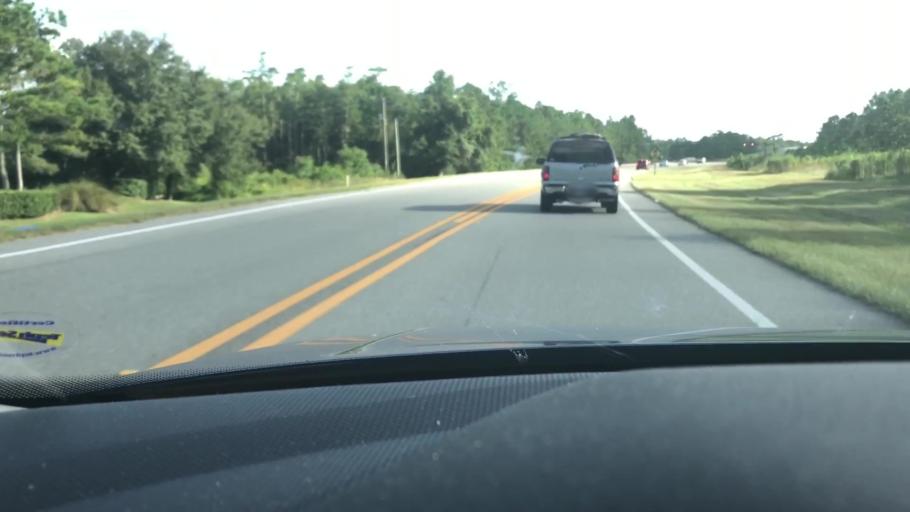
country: US
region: Florida
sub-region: Volusia County
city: Port Orange
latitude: 29.1289
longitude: -81.0474
